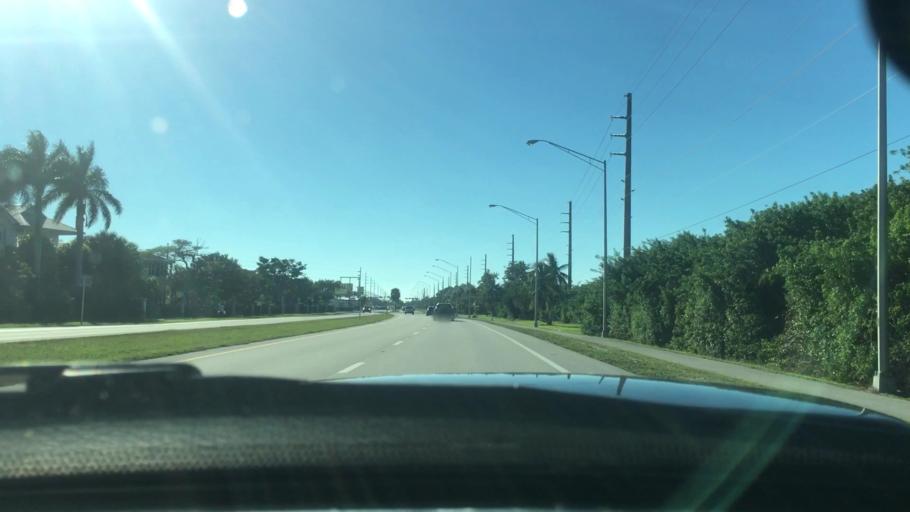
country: US
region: Florida
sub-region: Monroe County
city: Stock Island
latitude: 24.5743
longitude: -81.7386
